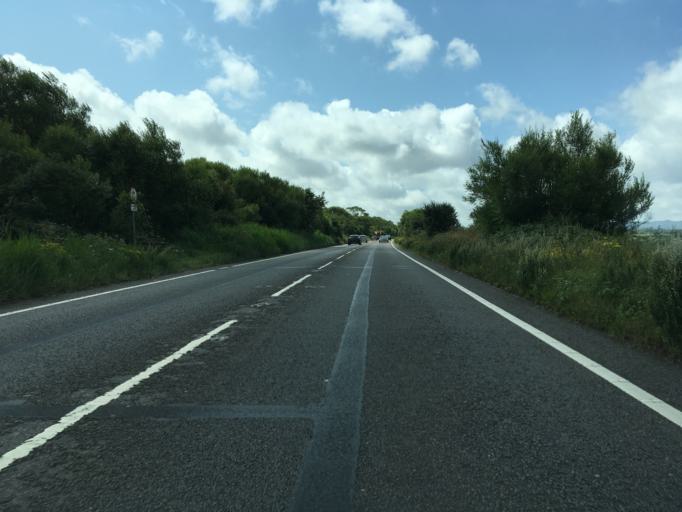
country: GB
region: England
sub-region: East Sussex
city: Pevensey
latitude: 50.8316
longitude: 0.3585
